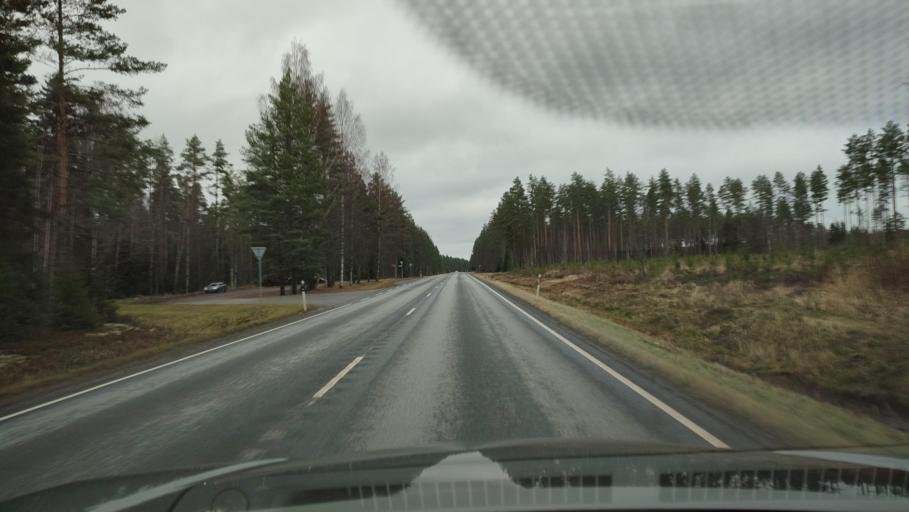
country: FI
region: Southern Ostrobothnia
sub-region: Suupohja
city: Kauhajoki
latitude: 62.5098
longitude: 22.3089
